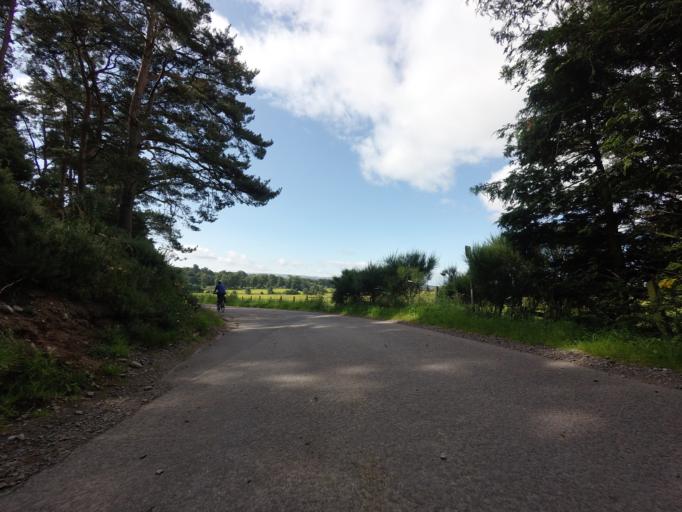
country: GB
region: Scotland
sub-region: Highland
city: Nairn
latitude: 57.5563
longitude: -3.8670
